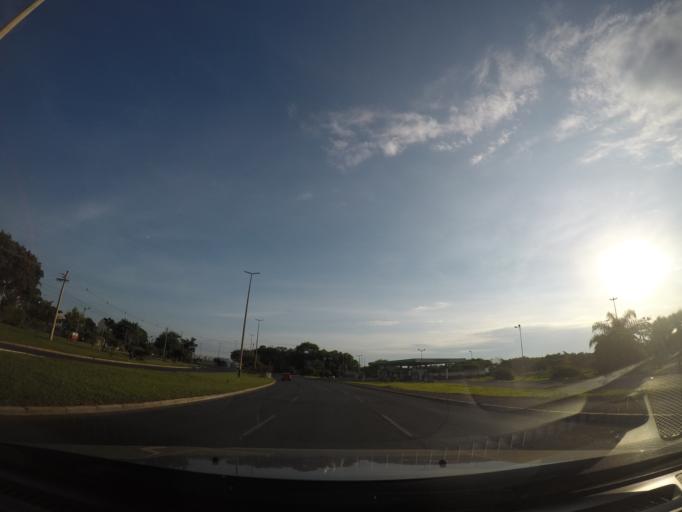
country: BR
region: Federal District
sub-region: Brasilia
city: Brasilia
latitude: -15.8454
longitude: -47.9671
